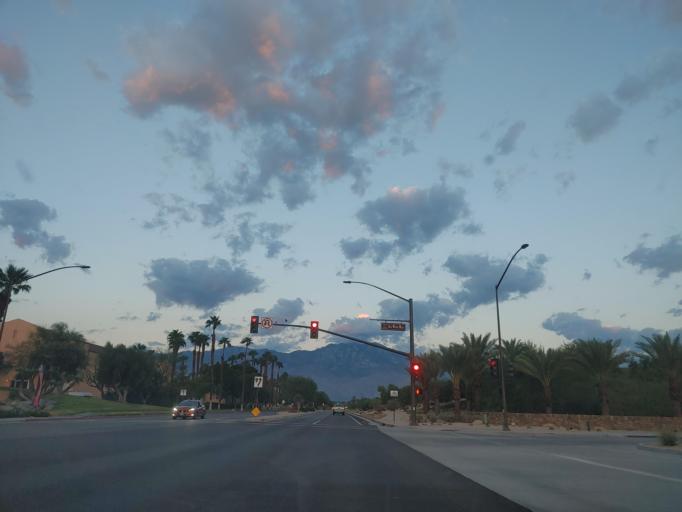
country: US
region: California
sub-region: Riverside County
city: Thousand Palms
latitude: 33.8017
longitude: -116.4173
